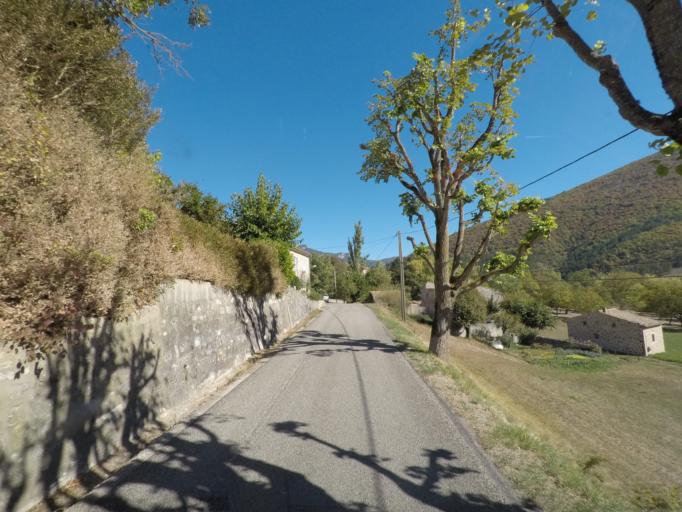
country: FR
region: Rhone-Alpes
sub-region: Departement de la Drome
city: Die
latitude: 44.6068
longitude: 5.2898
